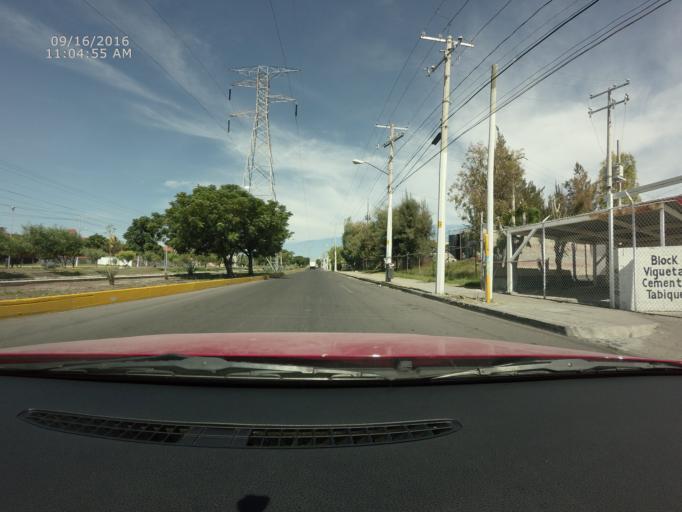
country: MX
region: Queretaro
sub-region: Queretaro
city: Sergio Villasenor
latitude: 20.6260
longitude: -100.4009
